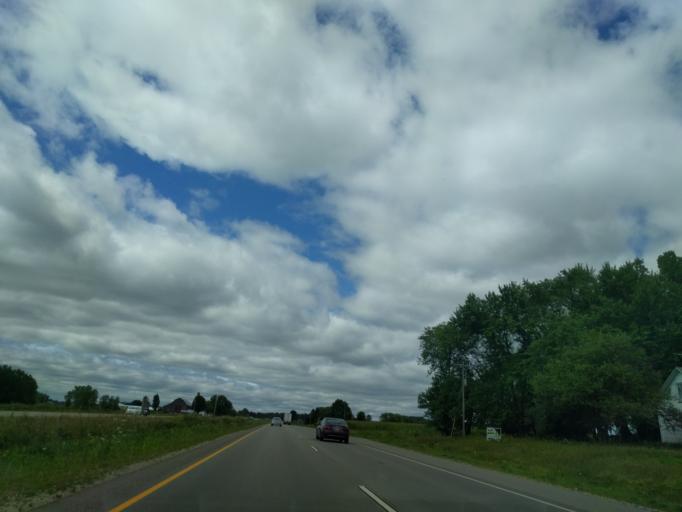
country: US
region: Wisconsin
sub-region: Oconto County
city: Oconto Falls
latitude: 44.8005
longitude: -88.0091
